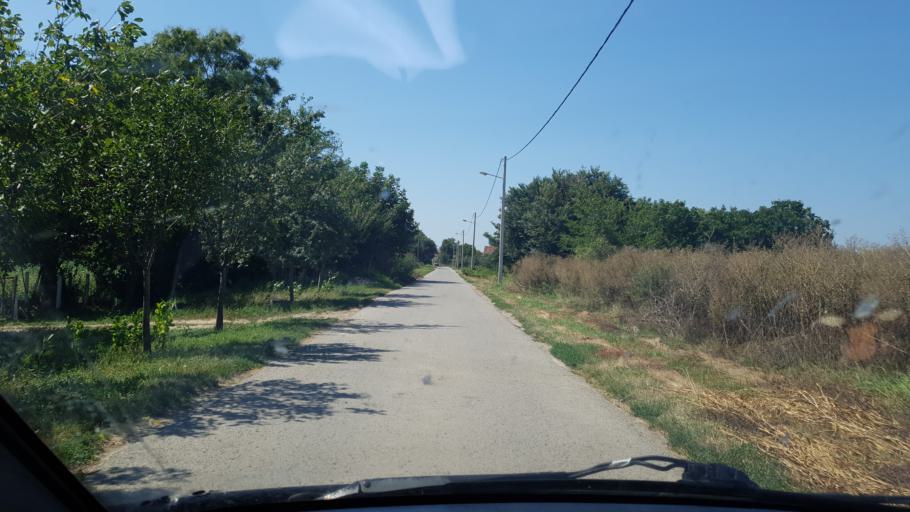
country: RS
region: Autonomna Pokrajina Vojvodina
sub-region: Juznobacki Okrug
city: Kovilj
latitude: 45.2235
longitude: 20.0298
